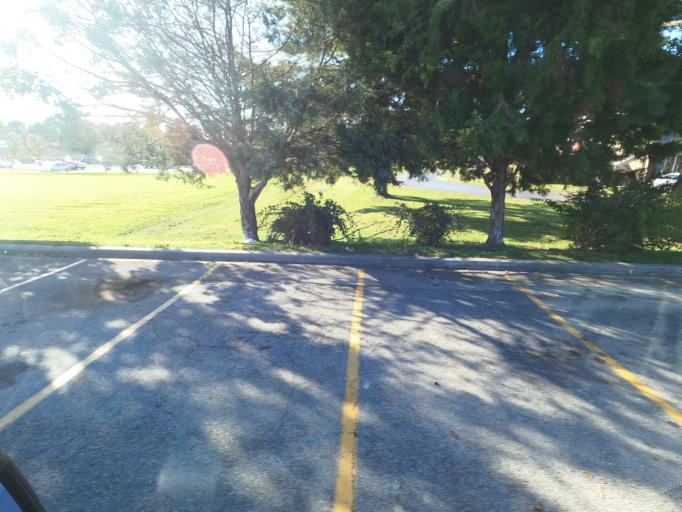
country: US
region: Tennessee
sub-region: Coffee County
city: Manchester
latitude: 35.4546
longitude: -86.0473
